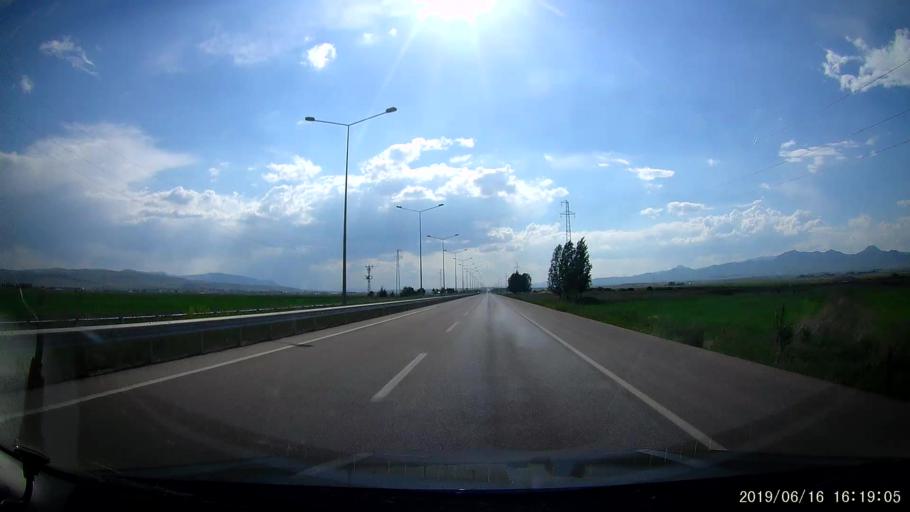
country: TR
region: Erzurum
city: Ilica
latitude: 39.9658
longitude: 41.1507
